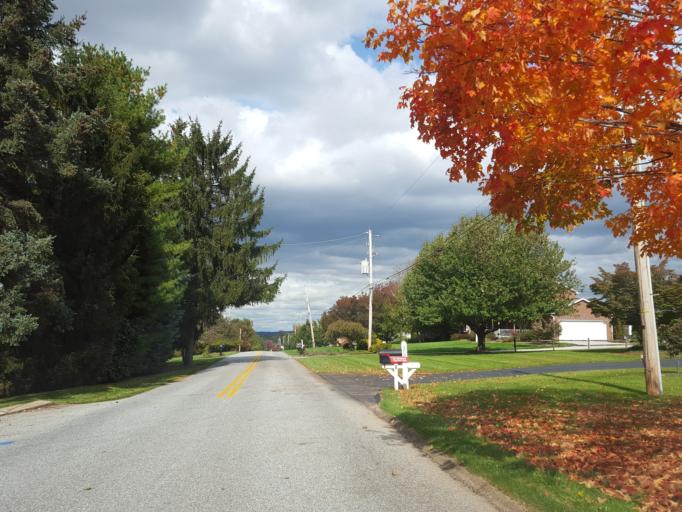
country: US
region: Pennsylvania
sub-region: York County
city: Spry
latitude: 39.9258
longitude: -76.6725
